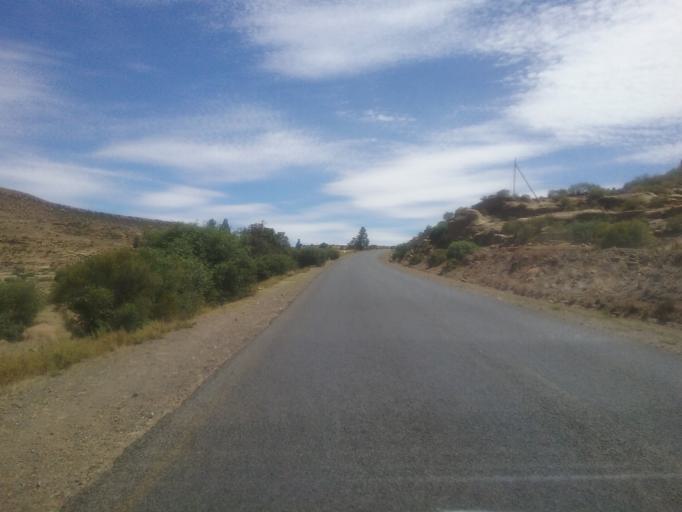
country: LS
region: Mohale's Hoek District
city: Mohale's Hoek
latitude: -30.0826
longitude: 27.4285
